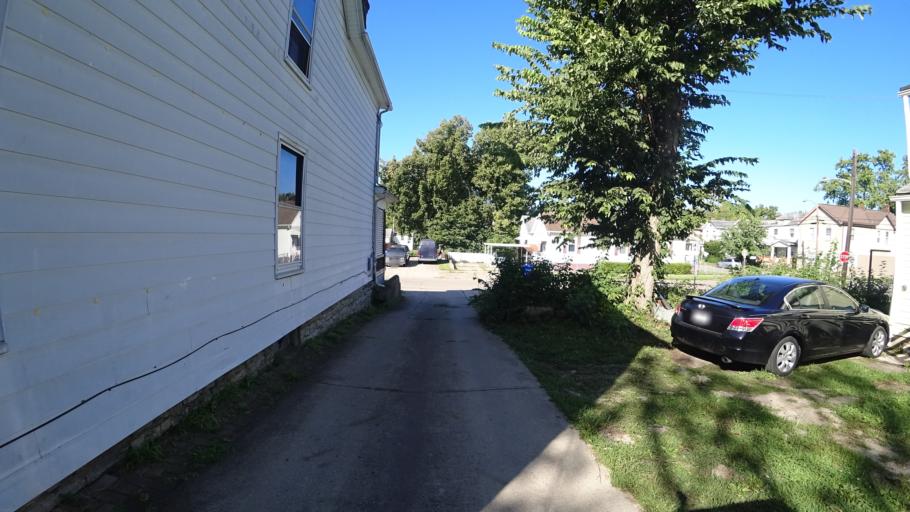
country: US
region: Ohio
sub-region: Butler County
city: Hamilton
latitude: 39.4028
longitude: -84.5489
